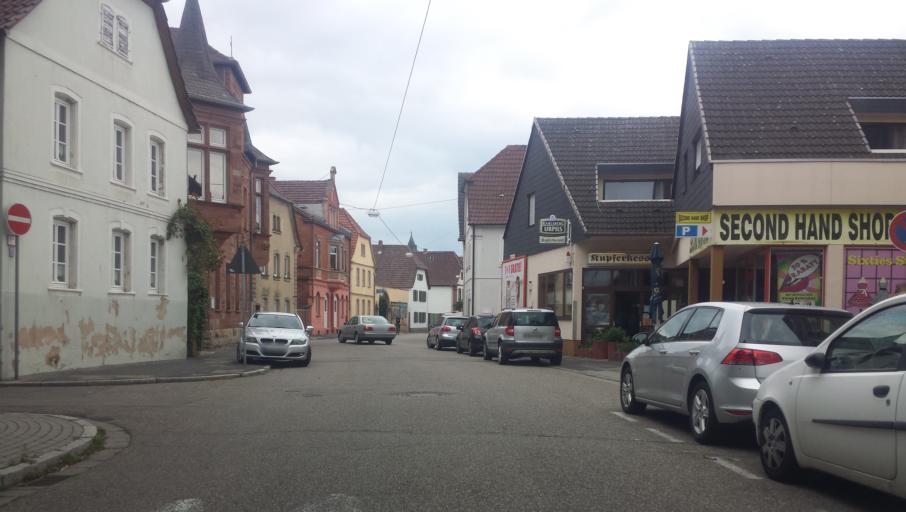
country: DE
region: Rheinland-Pfalz
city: Landau in der Pfalz
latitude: 49.1959
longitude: 8.1390
